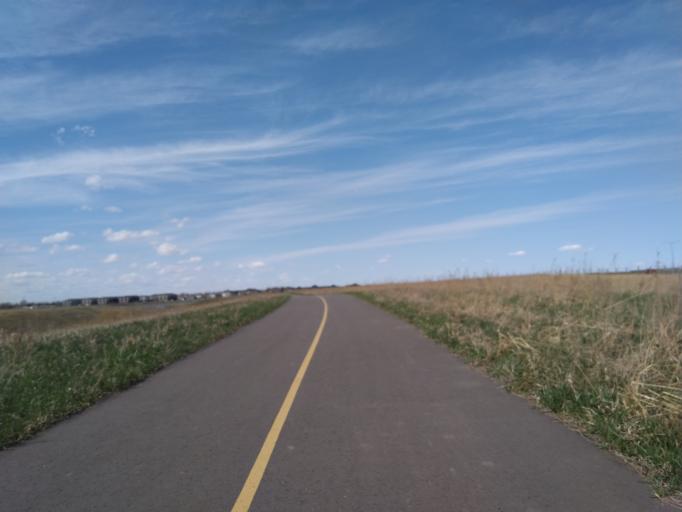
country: CA
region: Alberta
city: Chestermere
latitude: 51.0287
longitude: -113.9232
